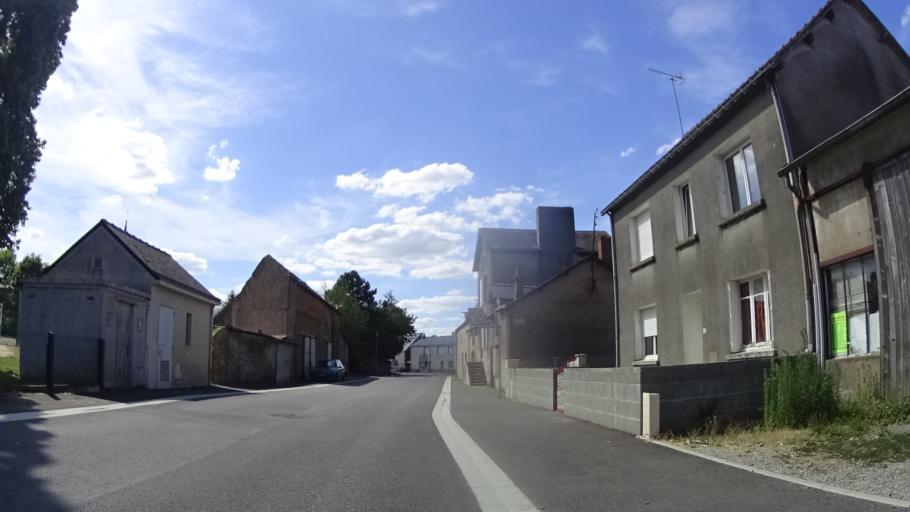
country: FR
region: Pays de la Loire
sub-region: Departement de la Loire-Atlantique
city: Saint-Mars-la-Jaille
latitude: 47.5750
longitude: -1.2035
